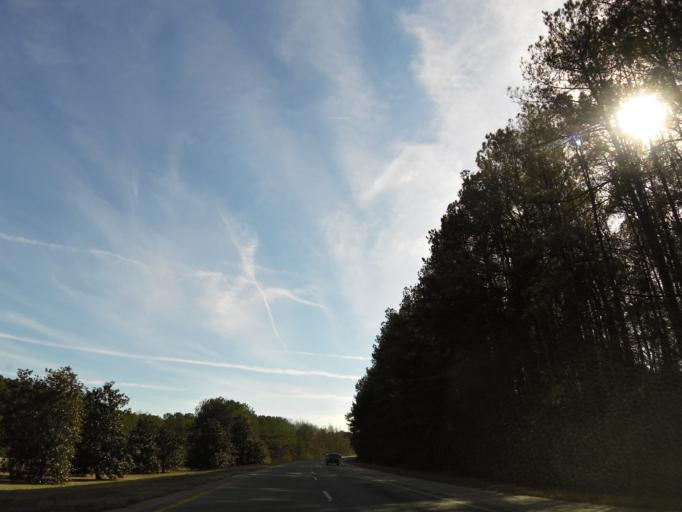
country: US
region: Georgia
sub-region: Troup County
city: La Grange
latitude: 32.9909
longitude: -84.9501
